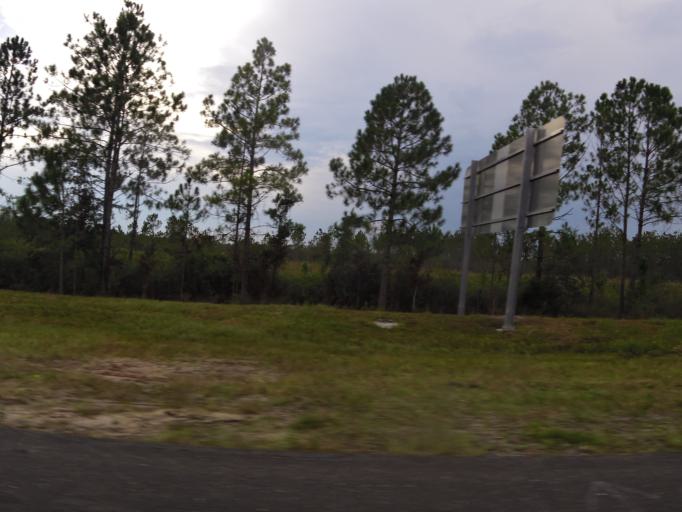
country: US
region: Florida
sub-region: Duval County
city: Baldwin
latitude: 30.2918
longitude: -81.8792
